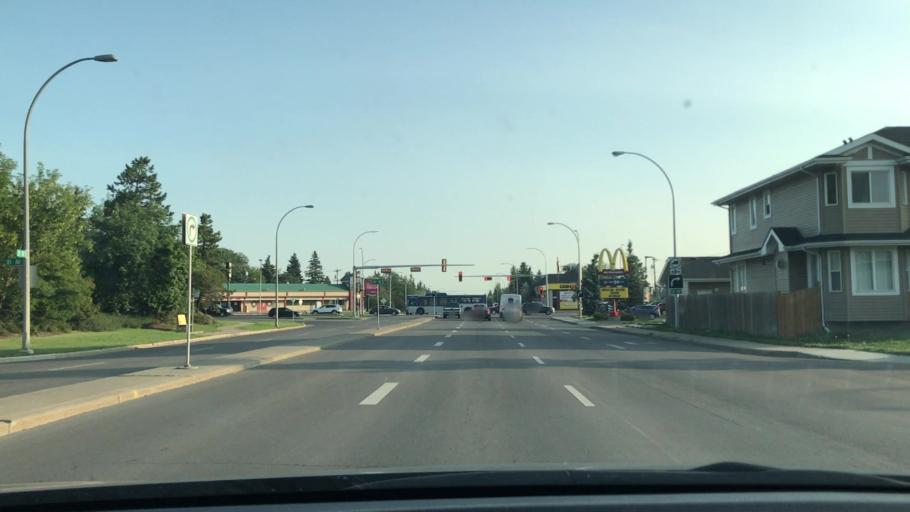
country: CA
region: Alberta
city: Edmonton
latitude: 53.5169
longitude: -113.4429
